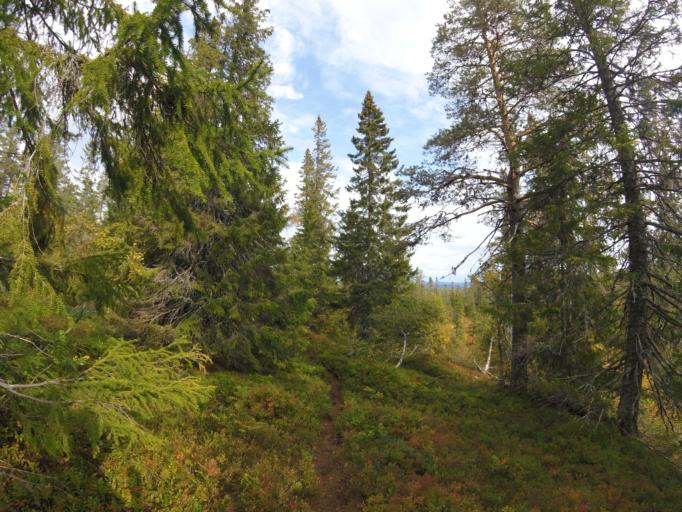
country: NO
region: Buskerud
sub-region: Rollag
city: Rollag
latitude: 59.8122
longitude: 9.3337
